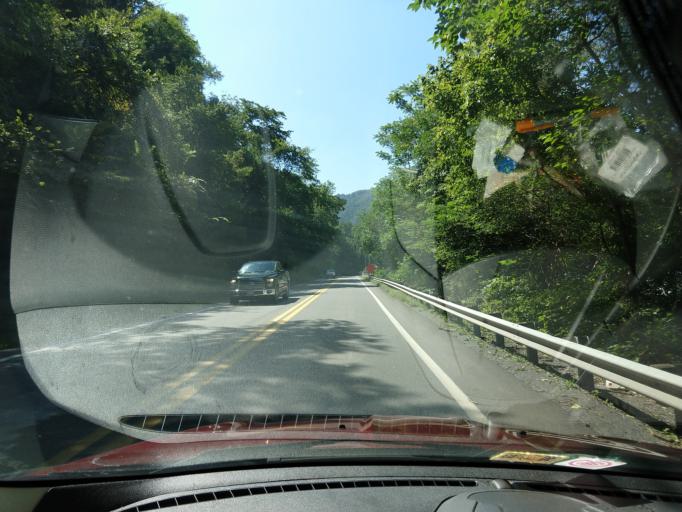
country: US
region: West Virginia
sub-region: Kanawha County
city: Montgomery
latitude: 38.1648
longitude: -81.3028
